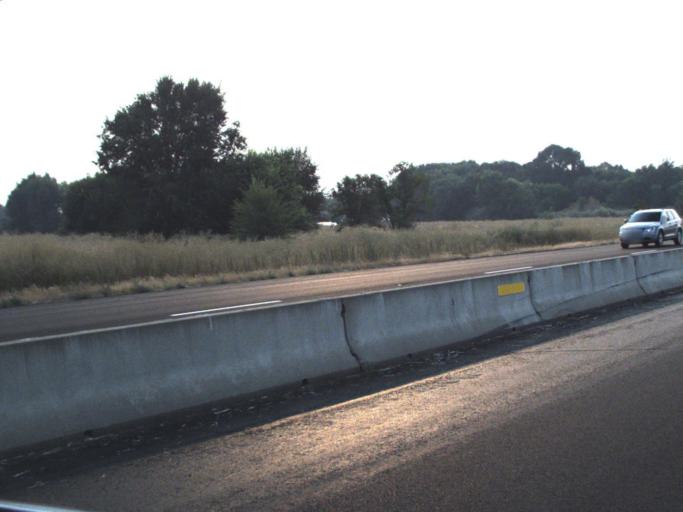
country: US
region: Washington
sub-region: Yakima County
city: Wapato
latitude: 46.4087
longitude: -120.3849
